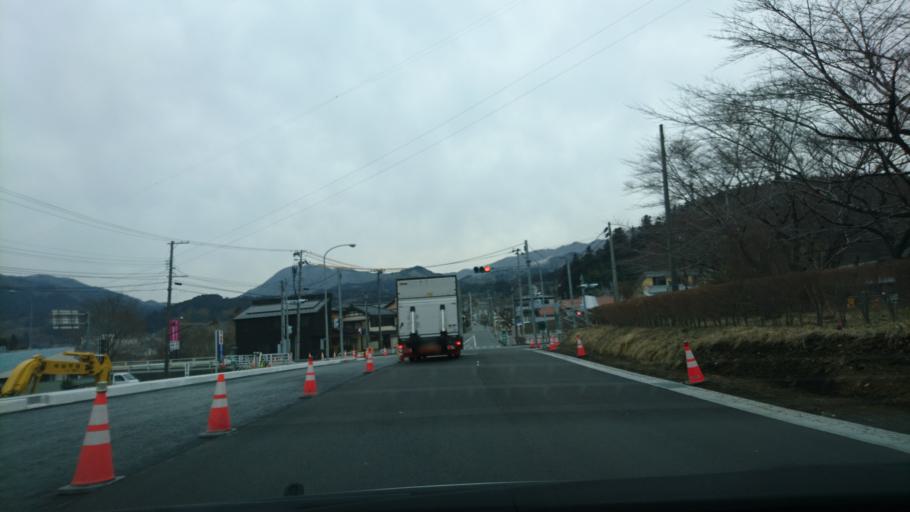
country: JP
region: Iwate
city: Ofunato
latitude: 39.1361
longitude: 141.5770
